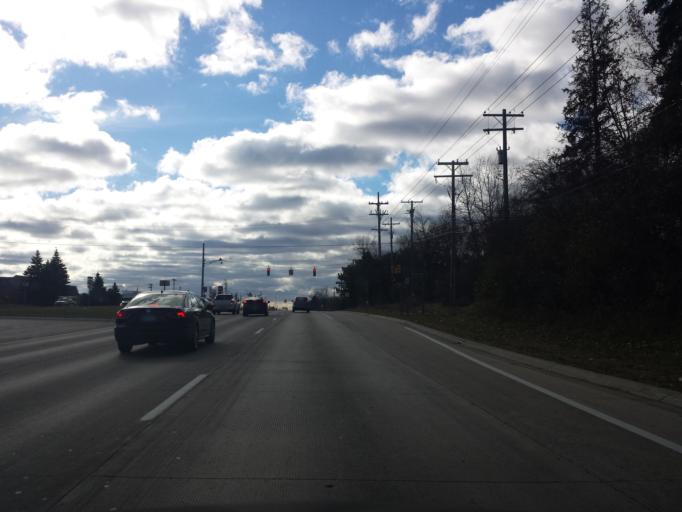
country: US
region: Michigan
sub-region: Oakland County
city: Bingham Farms
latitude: 42.5180
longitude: -83.2861
